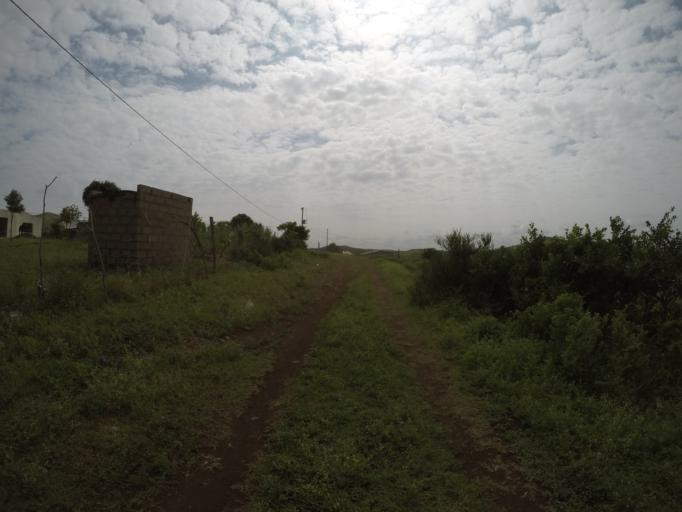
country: ZA
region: KwaZulu-Natal
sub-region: uThungulu District Municipality
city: Empangeni
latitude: -28.6191
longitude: 31.9070
